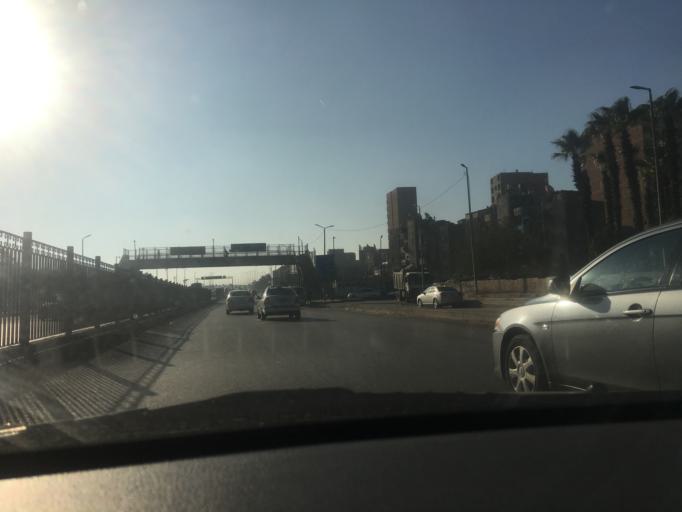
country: EG
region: Muhafazat al Qahirah
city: Cairo
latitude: 30.0141
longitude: 31.2664
